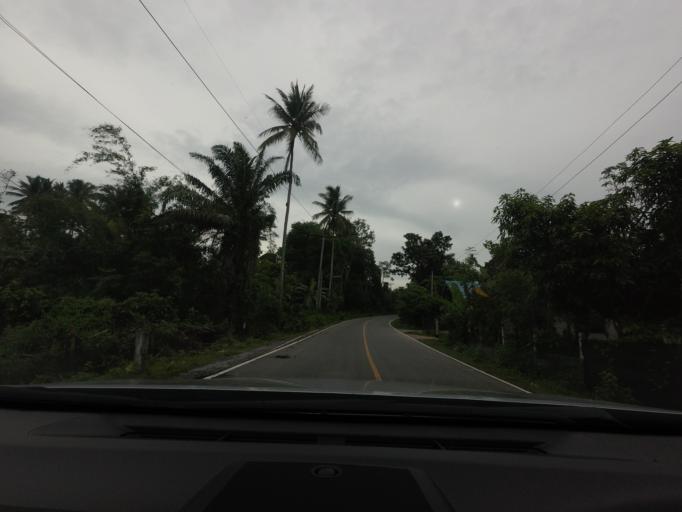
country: TH
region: Narathiwat
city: Rueso
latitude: 6.4136
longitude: 101.5195
